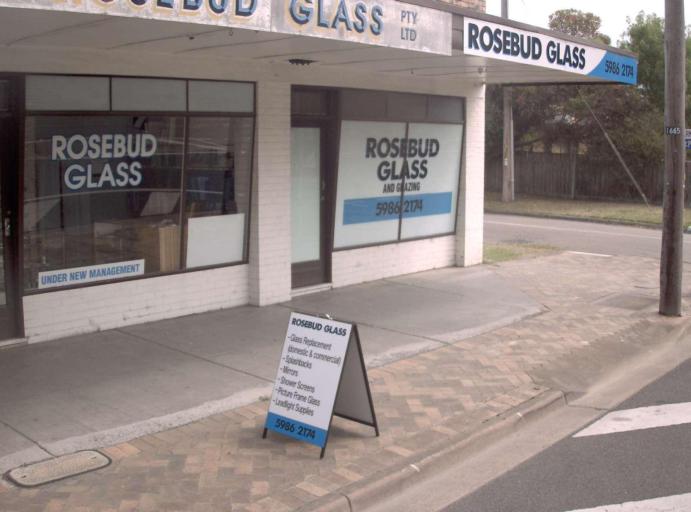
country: AU
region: Victoria
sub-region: Mornington Peninsula
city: Rosebud West
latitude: -38.3639
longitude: 144.8754
